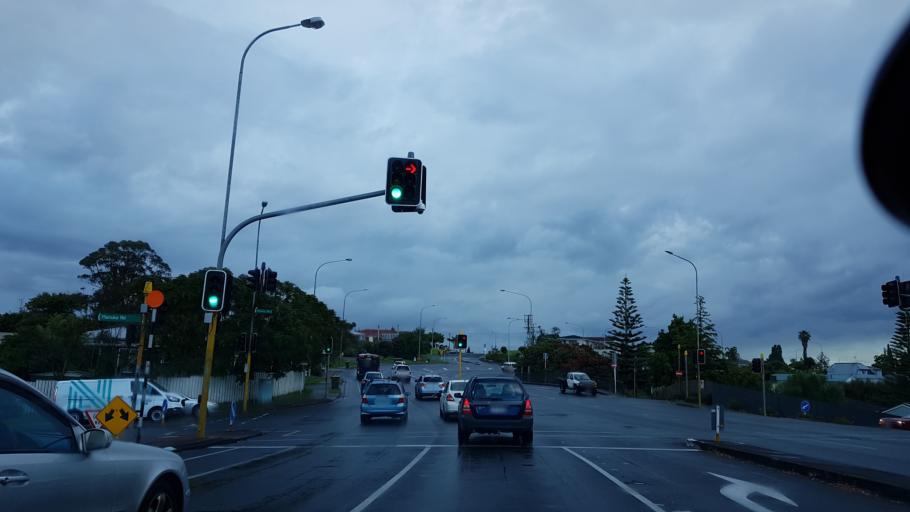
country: NZ
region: Auckland
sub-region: Auckland
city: North Shore
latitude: -36.7744
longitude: 174.7213
